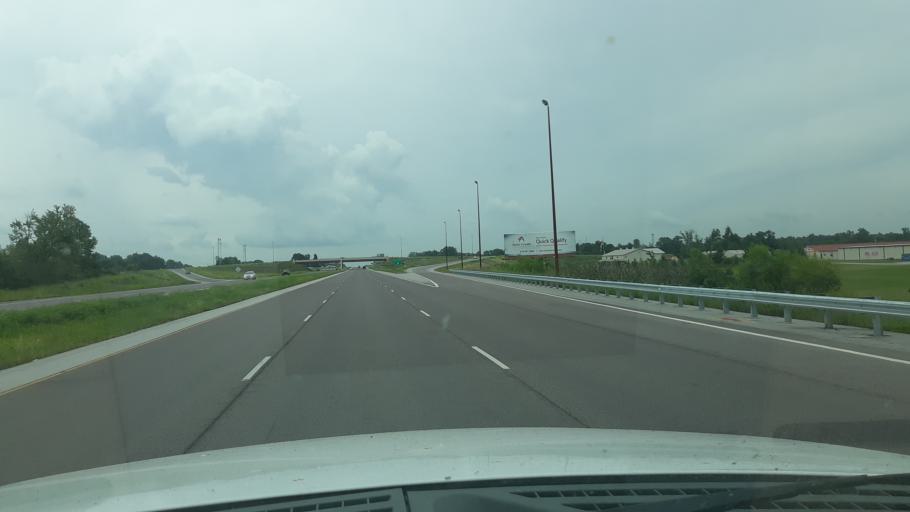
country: US
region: Illinois
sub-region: Williamson County
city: Crainville
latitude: 37.7450
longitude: -89.0646
